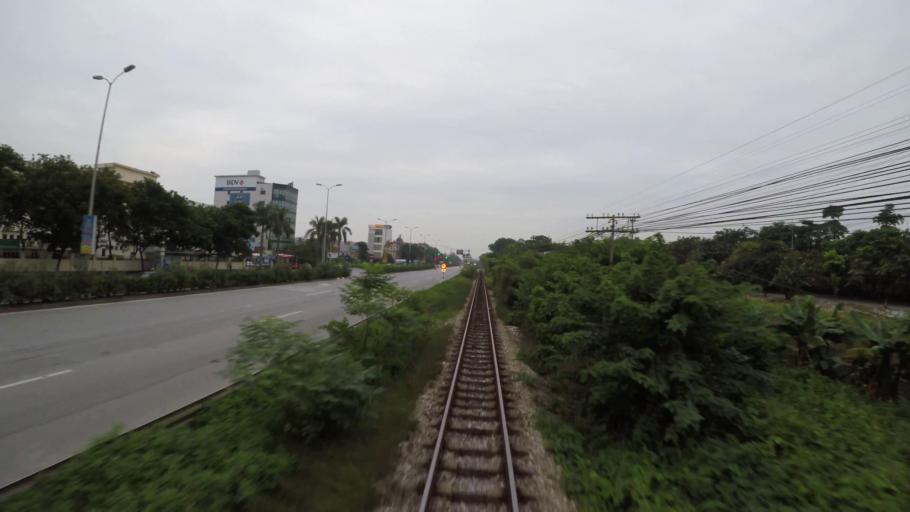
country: VN
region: Ha Noi
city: Trau Quy
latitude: 21.0046
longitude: 105.9608
